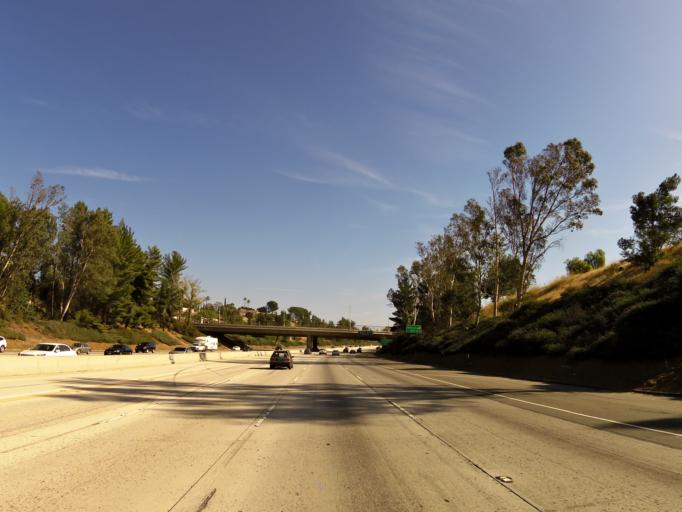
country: US
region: California
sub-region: Los Angeles County
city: Northridge
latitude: 34.2735
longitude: -118.5490
